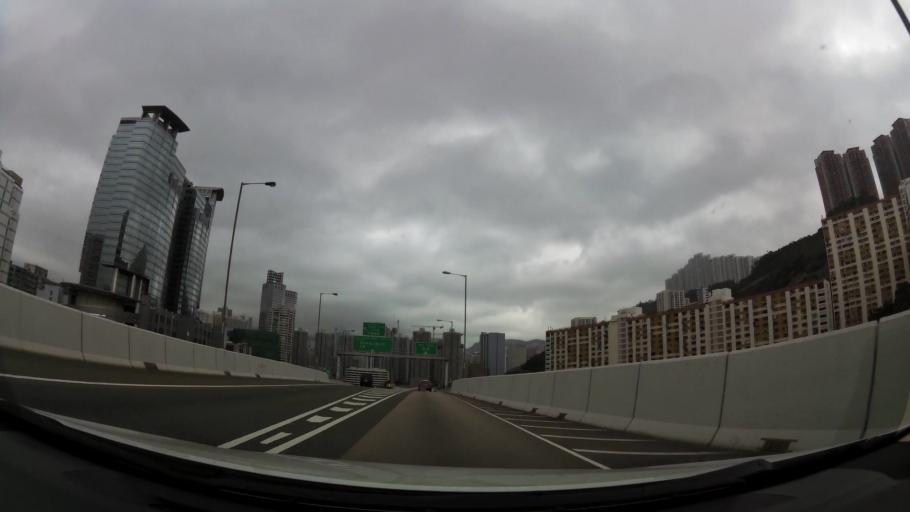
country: HK
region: Tsuen Wan
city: Tsuen Wan
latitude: 22.3505
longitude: 114.1247
